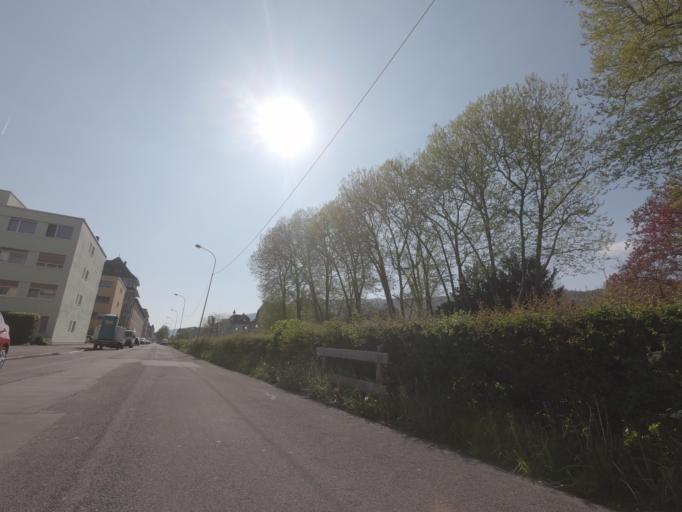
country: CH
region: Bern
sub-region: Biel/Bienne District
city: Biel/Bienne
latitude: 47.1406
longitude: 7.2548
